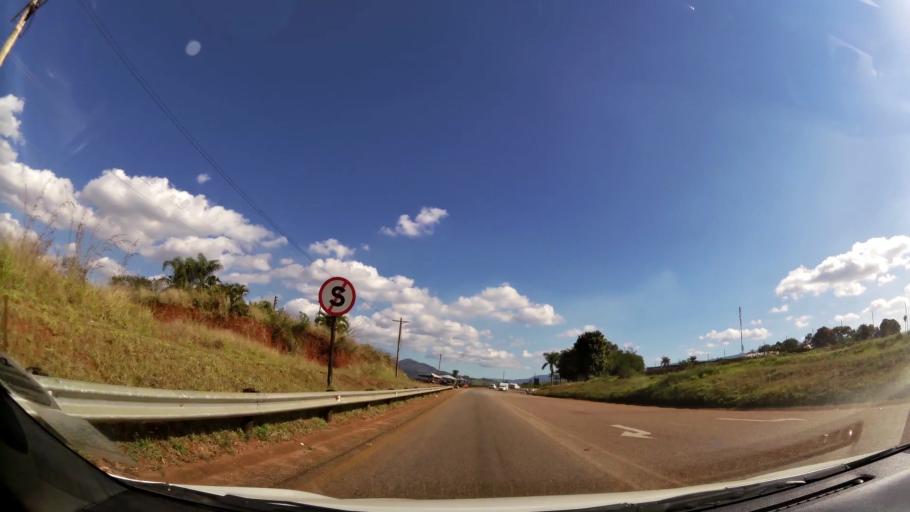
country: ZA
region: Limpopo
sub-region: Mopani District Municipality
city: Tzaneen
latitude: -23.8019
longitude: 30.1240
